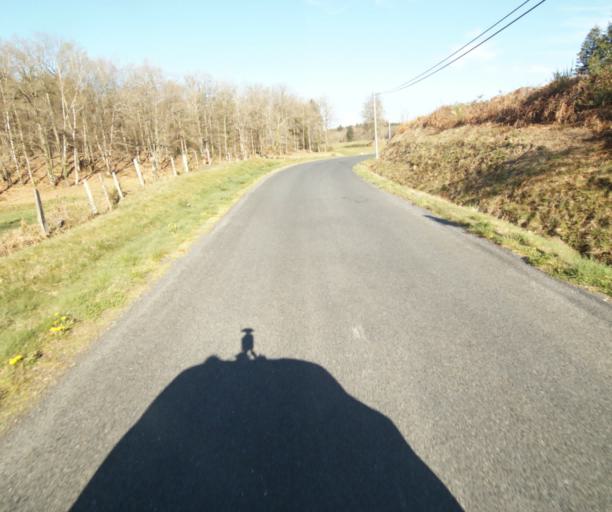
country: FR
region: Limousin
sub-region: Departement de la Correze
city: Correze
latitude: 45.2864
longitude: 1.8732
